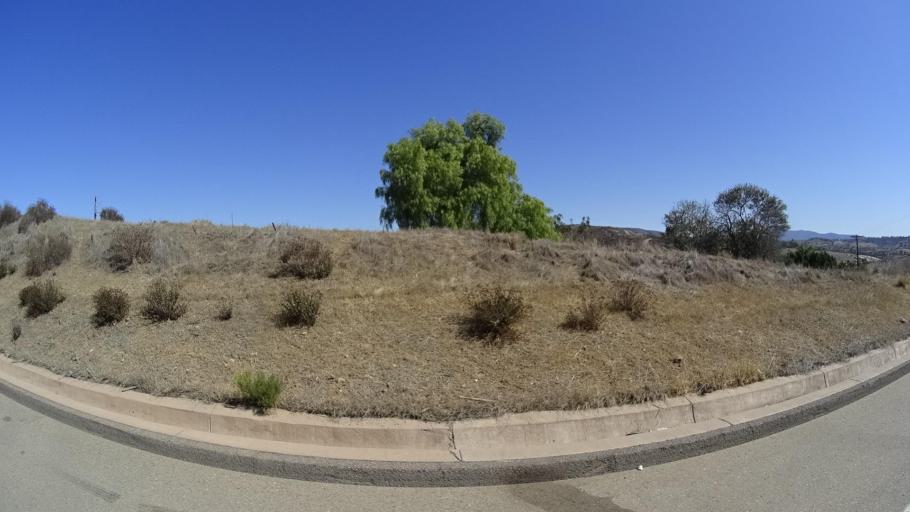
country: US
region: California
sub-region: San Diego County
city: La Presa
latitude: 32.6889
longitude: -117.0163
